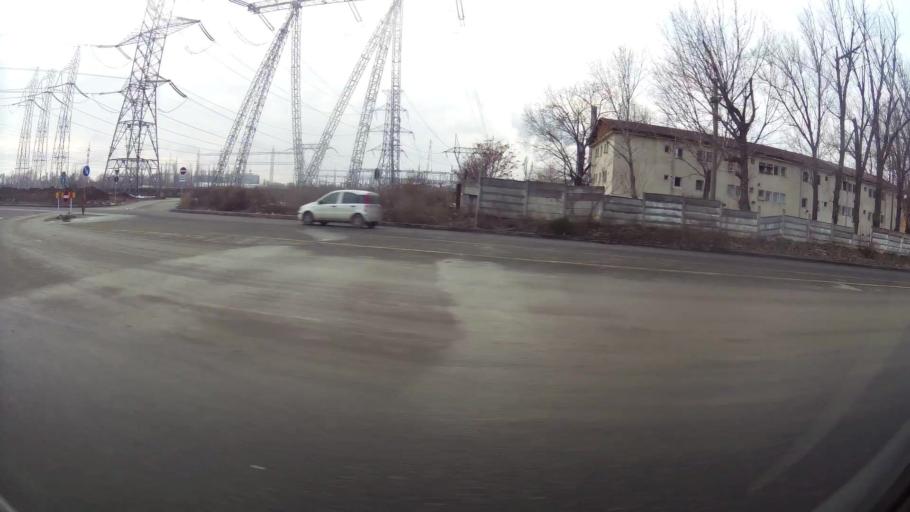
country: RO
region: Ilfov
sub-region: Comuna Popesti-Leordeni
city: Popesti-Leordeni
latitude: 44.4020
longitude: 26.1614
